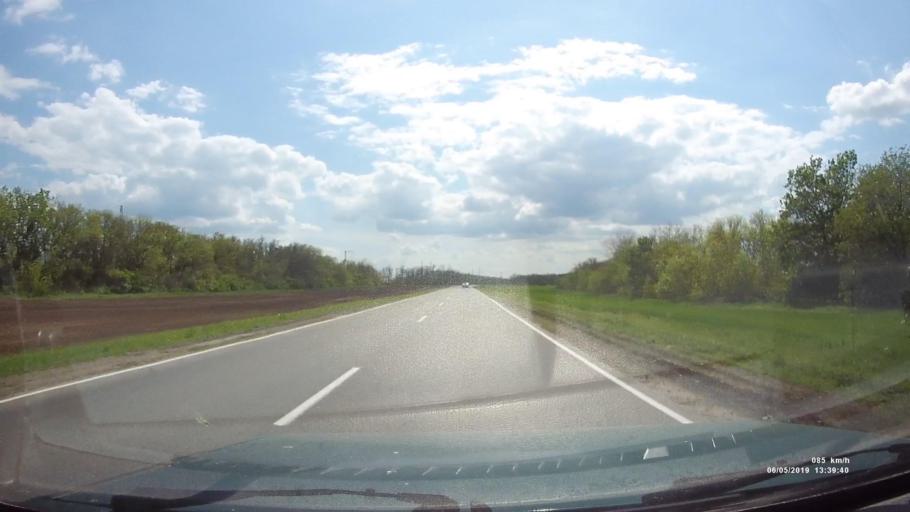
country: RU
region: Rostov
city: Ust'-Donetskiy
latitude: 47.6730
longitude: 40.7010
